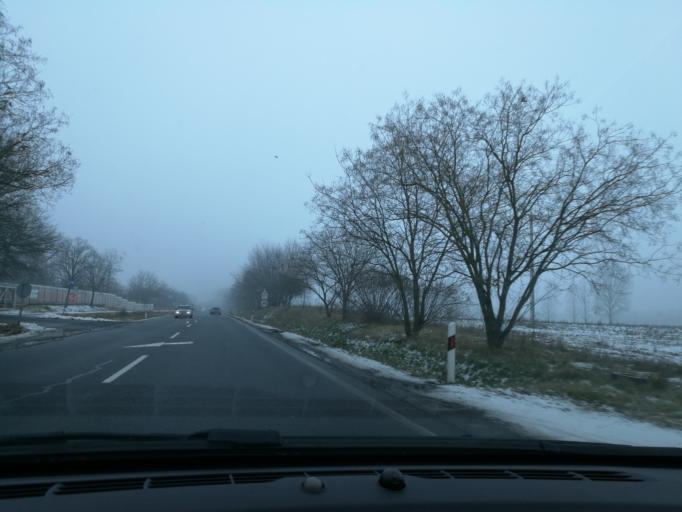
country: HU
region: Szabolcs-Szatmar-Bereg
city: Nyirpazony
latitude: 47.9958
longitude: 21.8090
